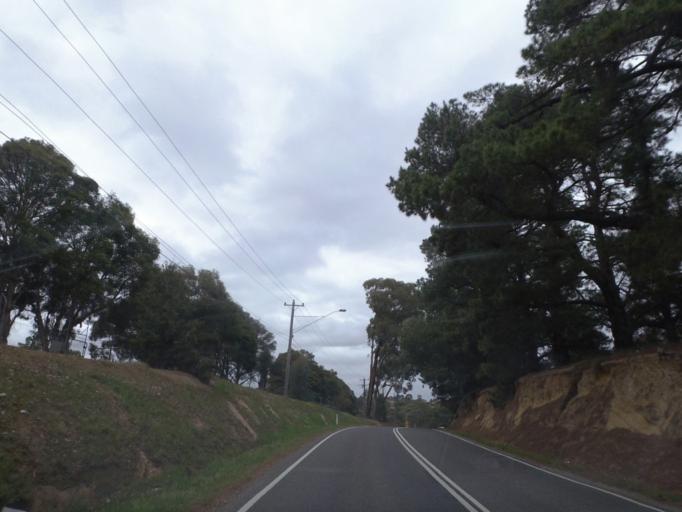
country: AU
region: Victoria
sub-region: Nillumbik
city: Eltham
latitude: -37.7515
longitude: 145.1705
